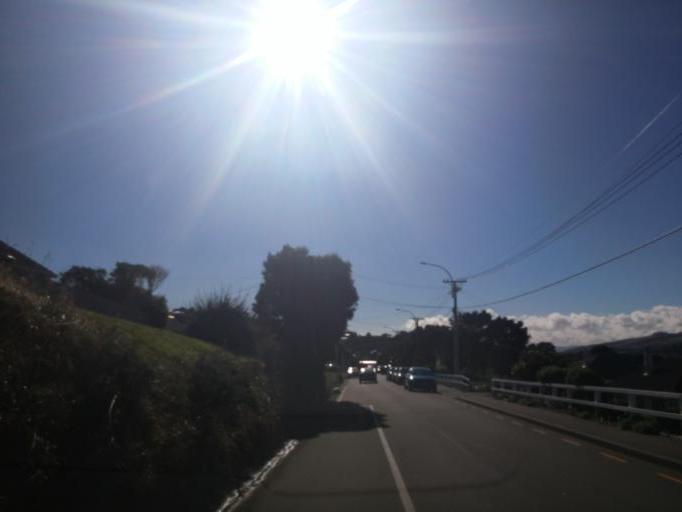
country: NZ
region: Wellington
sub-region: Wellington City
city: Wellington
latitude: -41.2272
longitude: 174.7995
